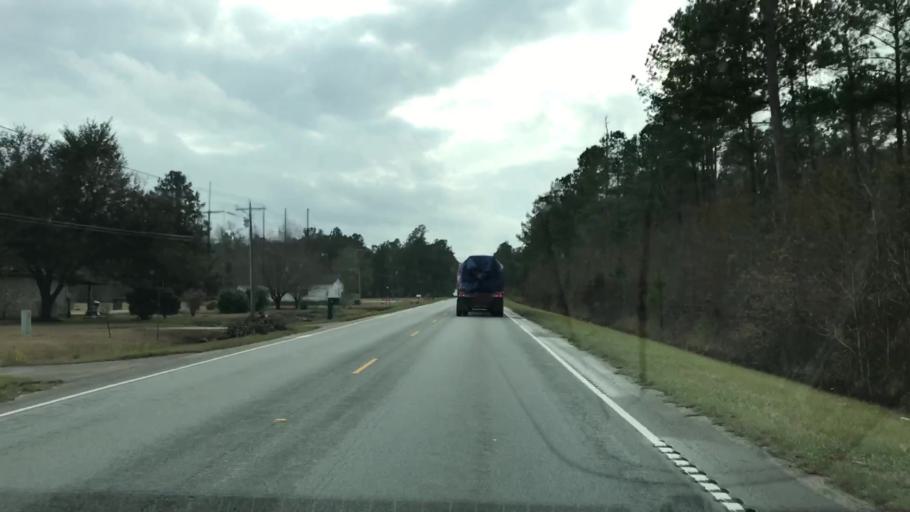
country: US
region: South Carolina
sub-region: Berkeley County
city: Bonneau Beach
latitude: 33.2615
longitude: -79.9270
